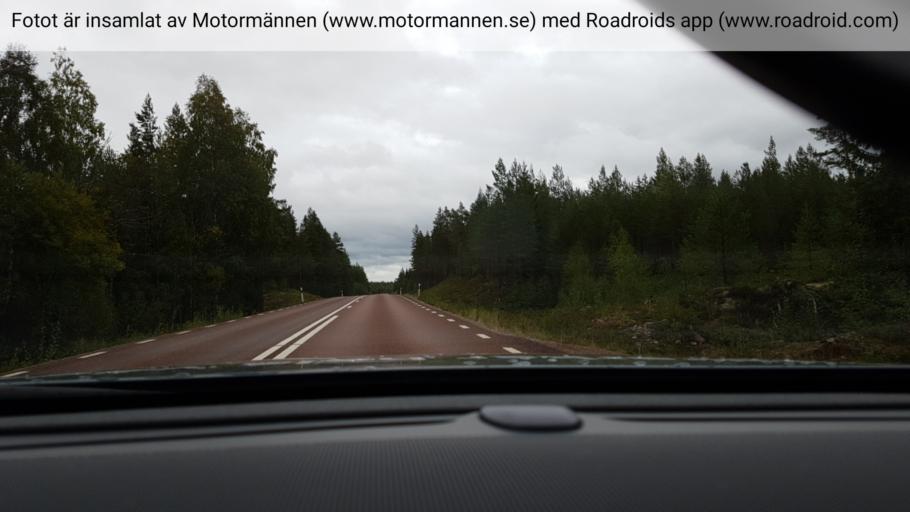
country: SE
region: Dalarna
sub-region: Malung-Saelens kommun
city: Malung
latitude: 60.8162
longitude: 13.8880
